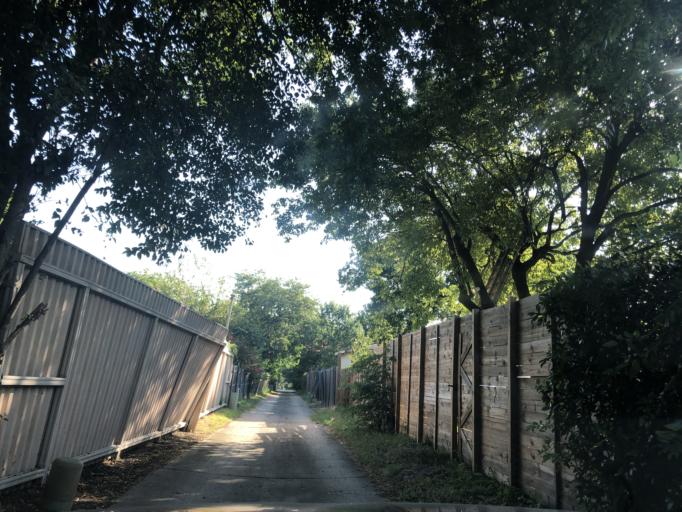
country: US
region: Texas
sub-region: Dallas County
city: Garland
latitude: 32.8609
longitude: -96.6316
